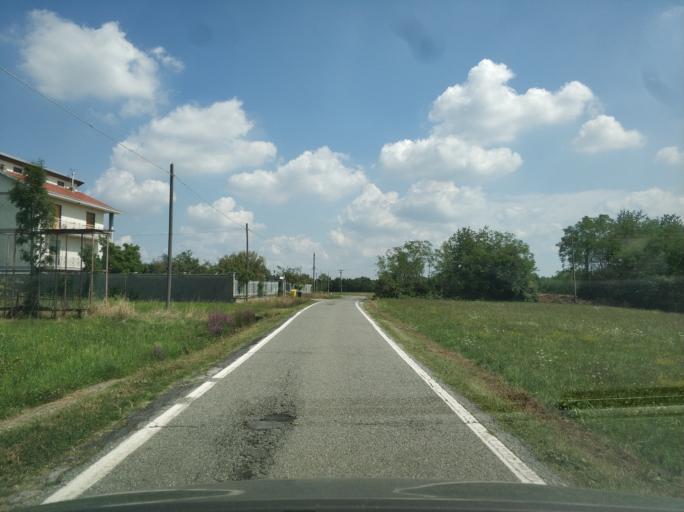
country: IT
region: Piedmont
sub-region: Provincia di Torino
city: San Francesco al Campo
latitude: 45.2499
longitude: 7.6714
